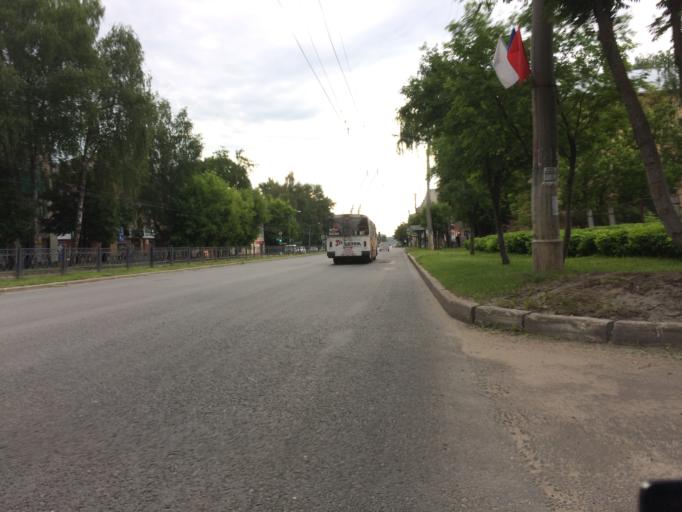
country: RU
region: Mariy-El
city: Yoshkar-Ola
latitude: 56.6429
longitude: 47.8834
